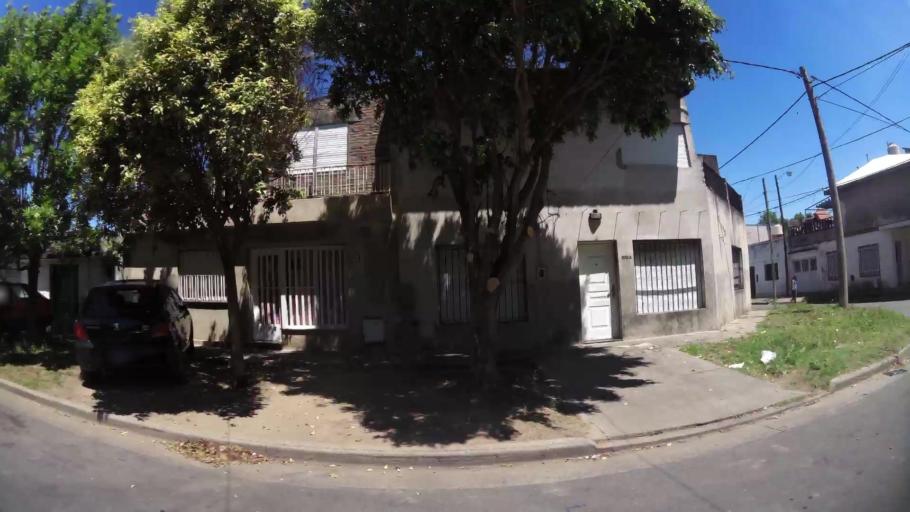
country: AR
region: Santa Fe
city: Perez
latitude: -32.9464
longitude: -60.7159
